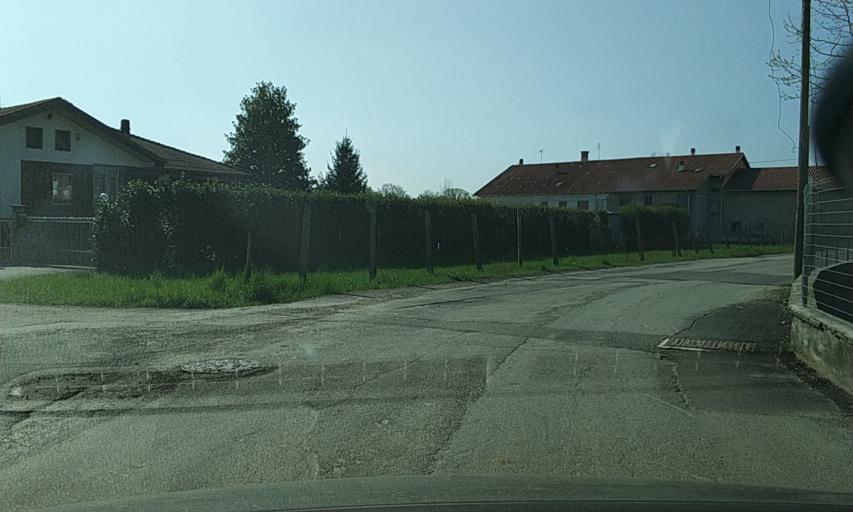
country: IT
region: Piedmont
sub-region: Provincia di Torino
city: Villanova Canavese
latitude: 45.2218
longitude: 7.5531
